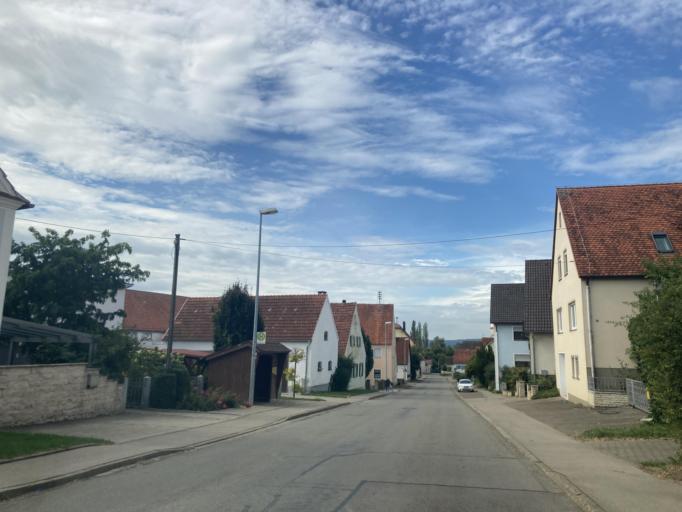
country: DE
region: Bavaria
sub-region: Swabia
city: Mottingen
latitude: 48.8190
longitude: 10.6081
